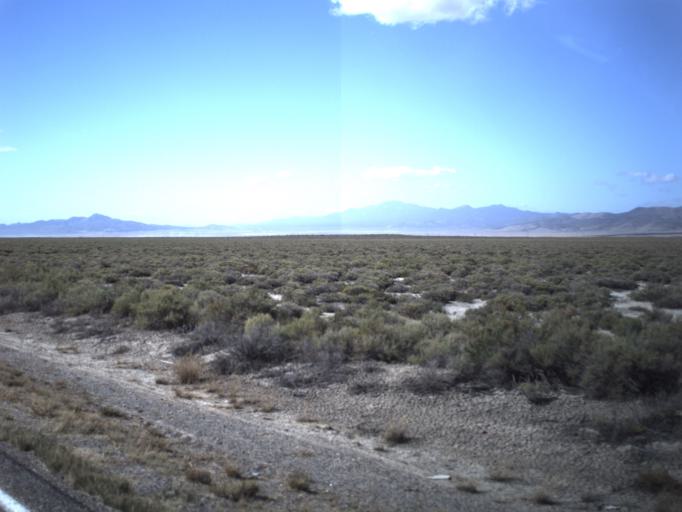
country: US
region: Utah
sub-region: Beaver County
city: Milford
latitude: 38.7072
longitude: -112.9708
